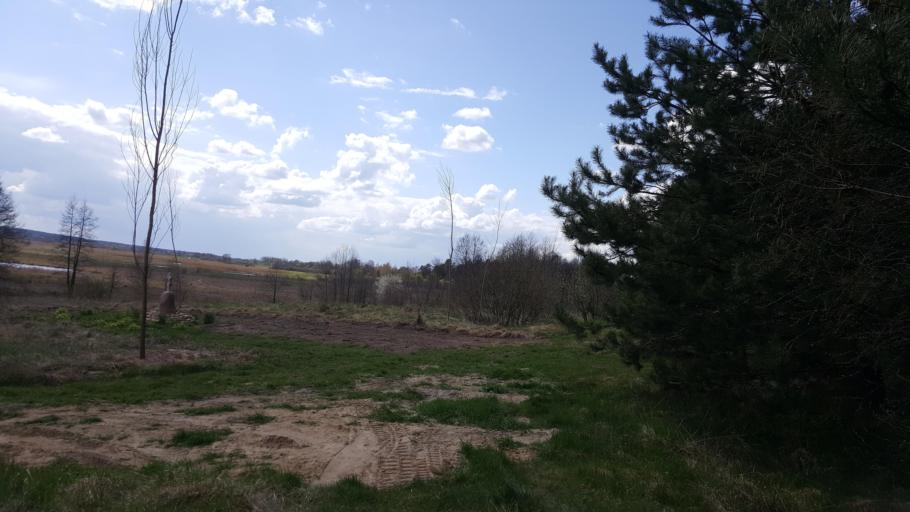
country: BY
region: Brest
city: Kamyanyets
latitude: 52.3528
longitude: 23.7022
